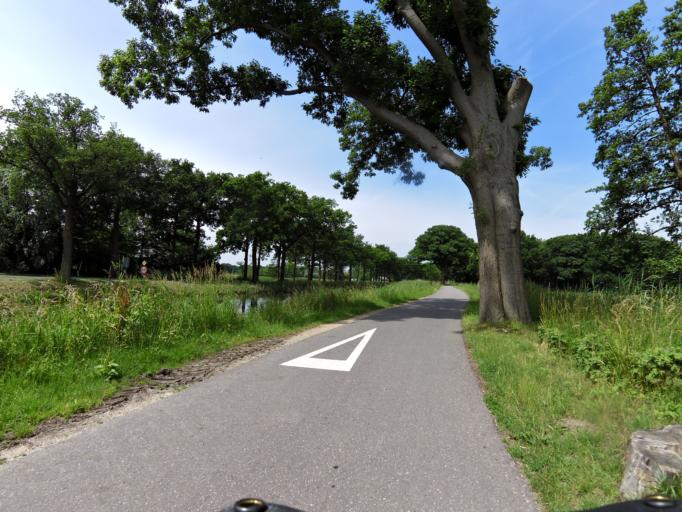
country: NL
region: Gelderland
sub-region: Gemeente Brummen
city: Eerbeek
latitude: 52.1254
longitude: 6.0500
